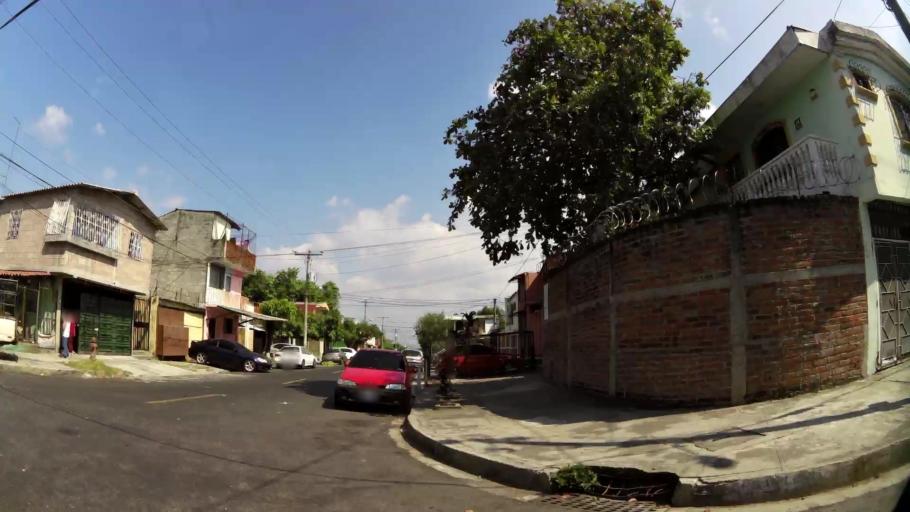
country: SV
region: San Salvador
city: Mejicanos
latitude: 13.7200
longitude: -89.2147
